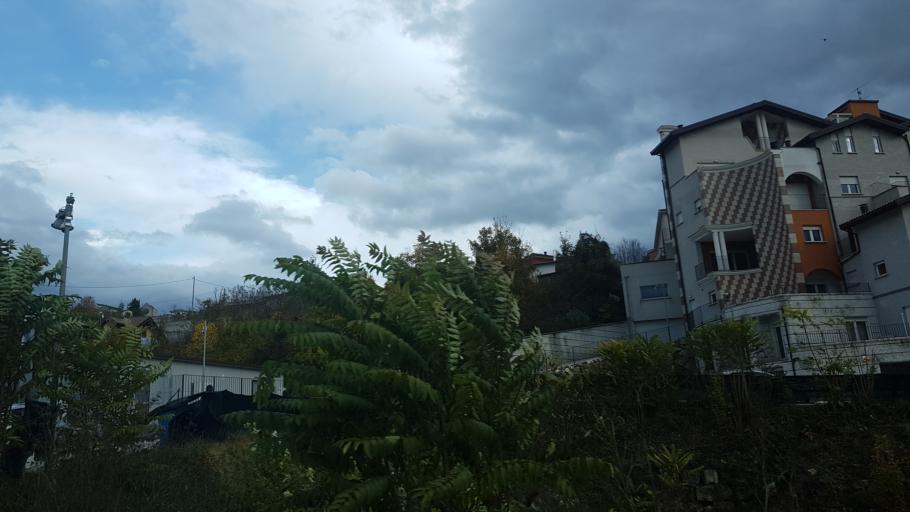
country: IT
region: Abruzzo
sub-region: Provincia dell' Aquila
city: L'Aquila
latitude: 42.3479
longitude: 13.4113
